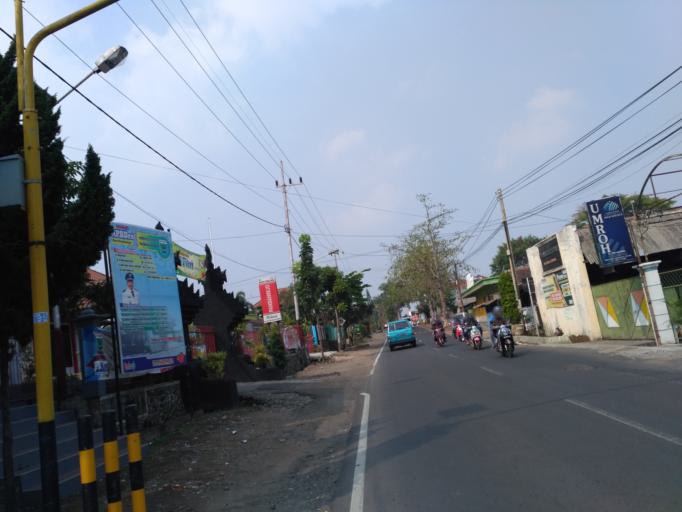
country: ID
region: East Java
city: Batu
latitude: -7.8646
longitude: 112.5397
